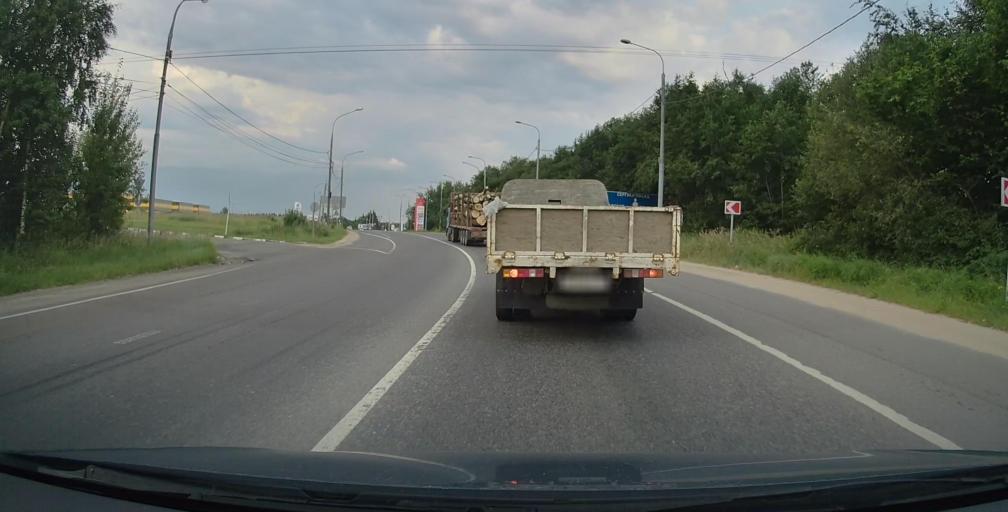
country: RU
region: Moskovskaya
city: Skoropuskovskiy
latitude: 56.3781
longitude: 38.1075
